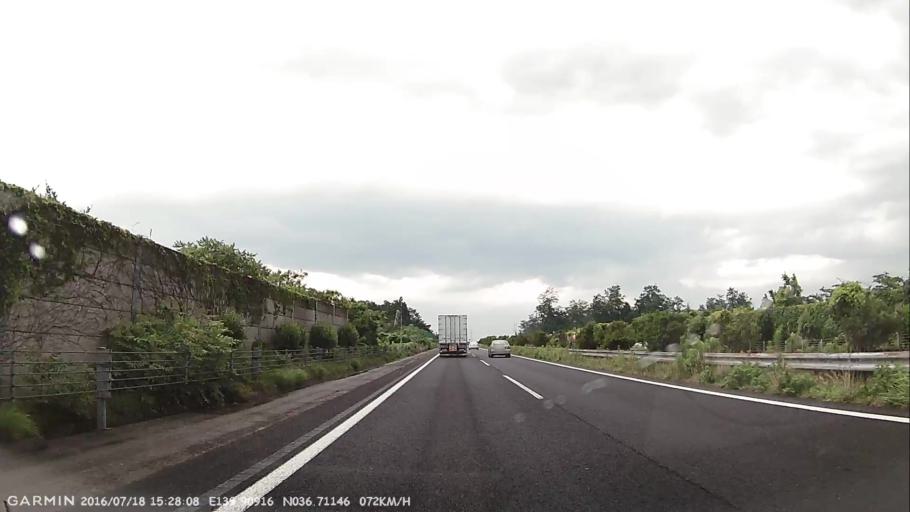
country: JP
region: Tochigi
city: Ujiie
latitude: 36.7115
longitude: 139.9092
